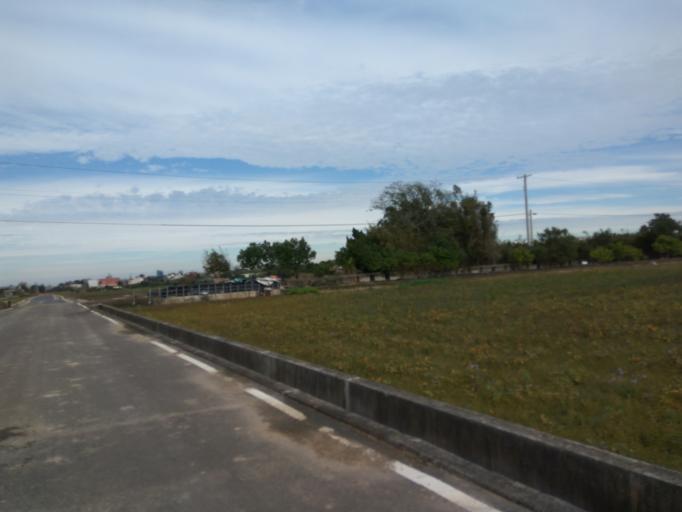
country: TW
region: Taiwan
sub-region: Hsinchu
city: Zhubei
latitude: 24.9523
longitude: 121.1038
